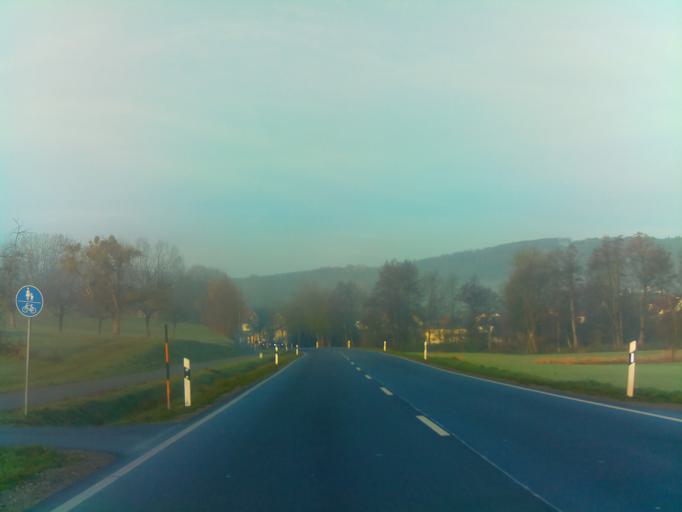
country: DE
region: Hesse
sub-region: Regierungsbezirk Darmstadt
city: Rimbach
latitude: 49.6459
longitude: 8.7479
